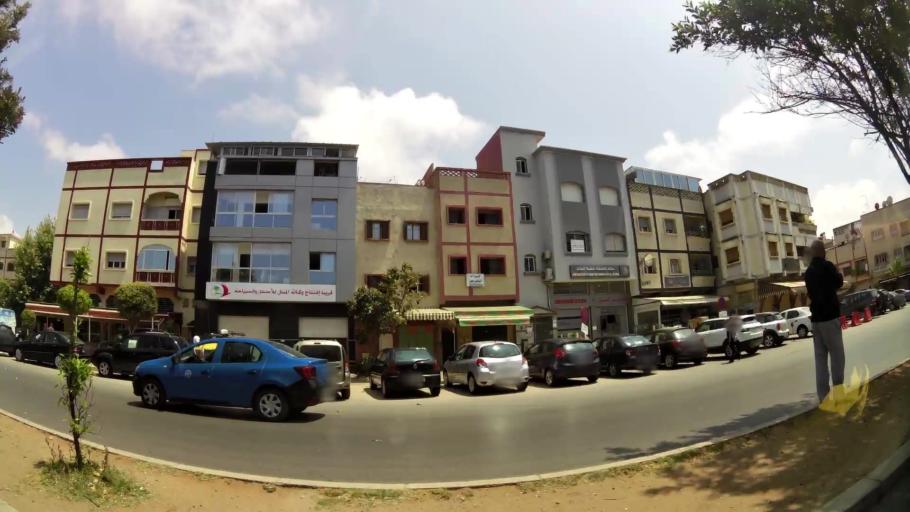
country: MA
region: Rabat-Sale-Zemmour-Zaer
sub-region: Skhirate-Temara
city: Temara
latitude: 33.9760
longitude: -6.8881
